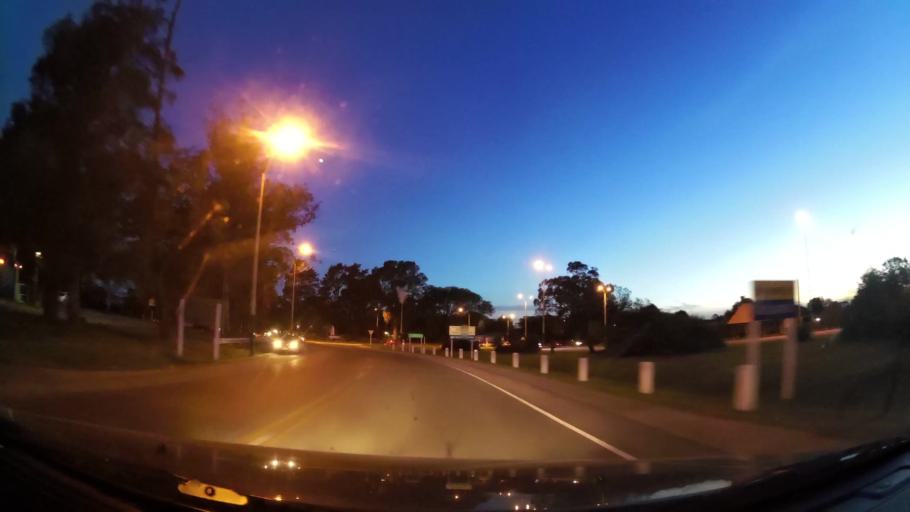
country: UY
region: Canelones
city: Atlantida
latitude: -34.7687
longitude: -55.7638
